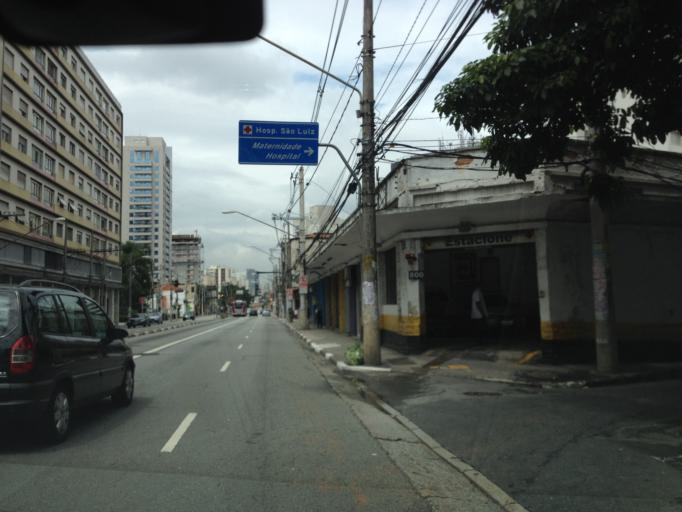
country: BR
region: Sao Paulo
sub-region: Sao Paulo
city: Sao Paulo
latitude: -23.5908
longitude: -46.6724
